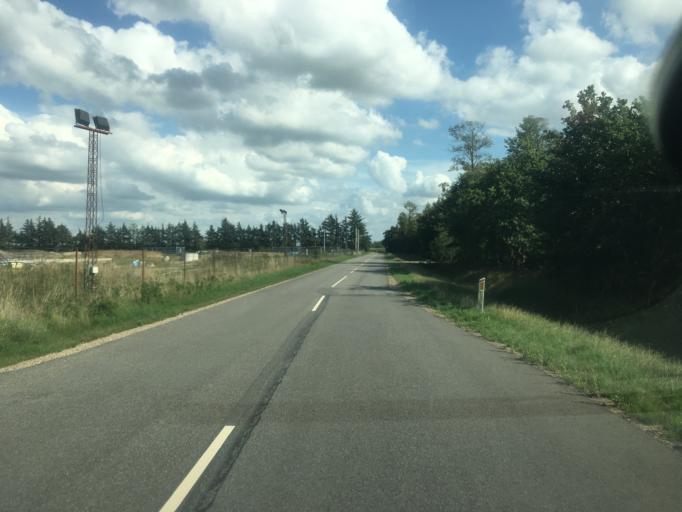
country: DE
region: Schleswig-Holstein
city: Ellhoft
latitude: 54.9666
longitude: 8.9737
